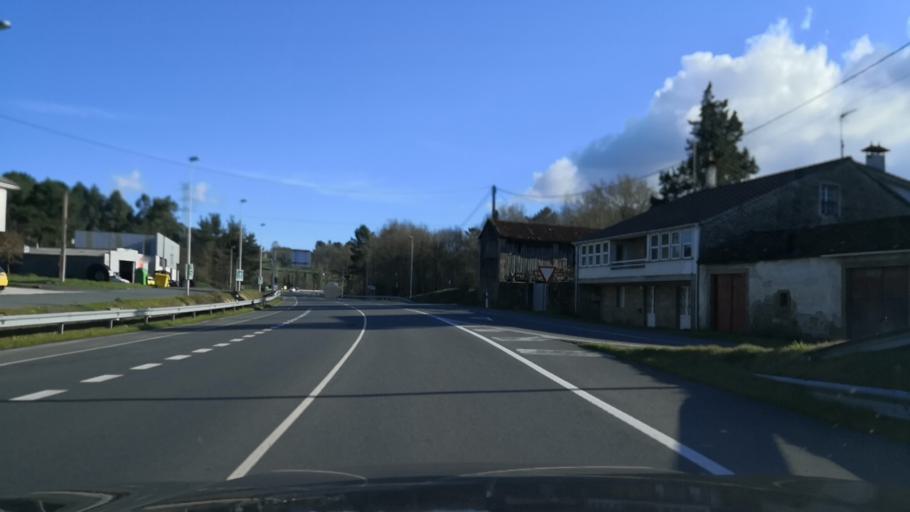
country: ES
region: Galicia
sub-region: Provincia de Pontevedra
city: Silleda
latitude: 42.7176
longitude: -8.2829
